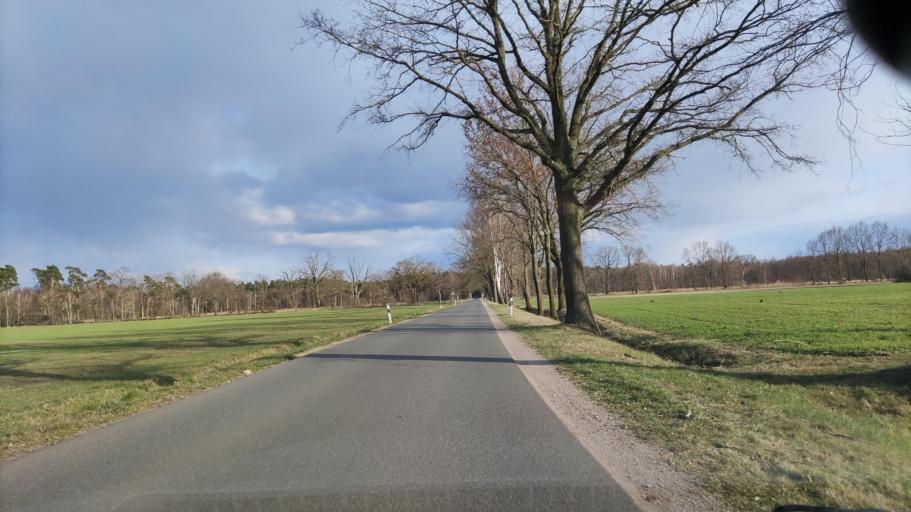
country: DE
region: Lower Saxony
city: Langendorf
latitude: 53.0503
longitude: 11.2344
